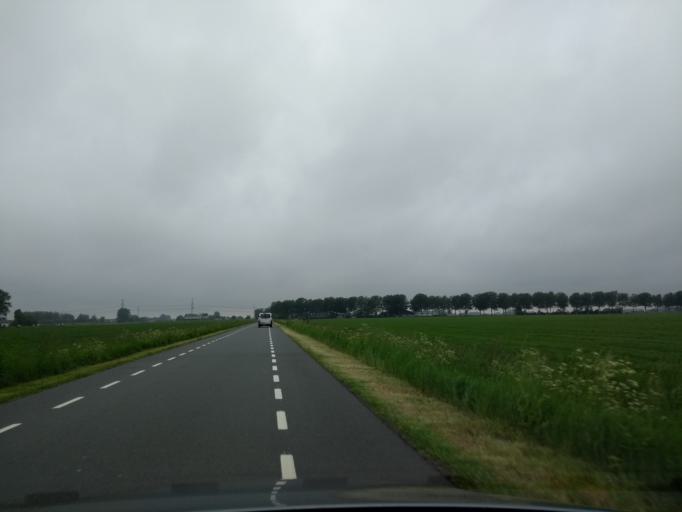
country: NL
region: Groningen
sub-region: Gemeente Zuidhorn
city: Aduard
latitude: 53.2601
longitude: 6.4955
